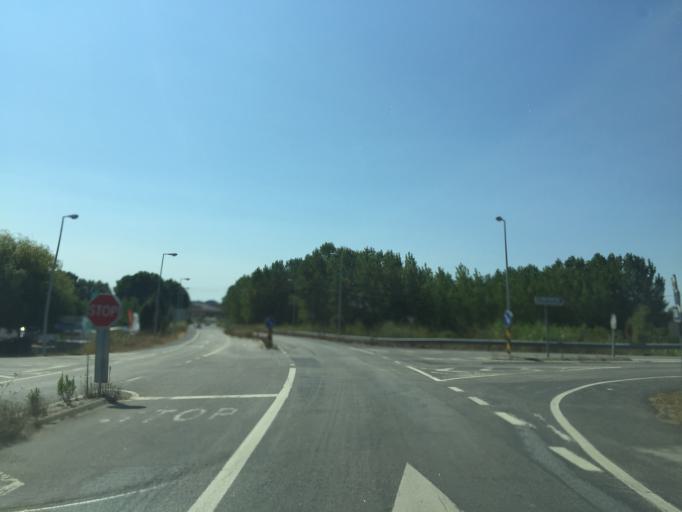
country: PT
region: Aveiro
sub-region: Mealhada
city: Mealhada
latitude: 40.3737
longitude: -8.4737
